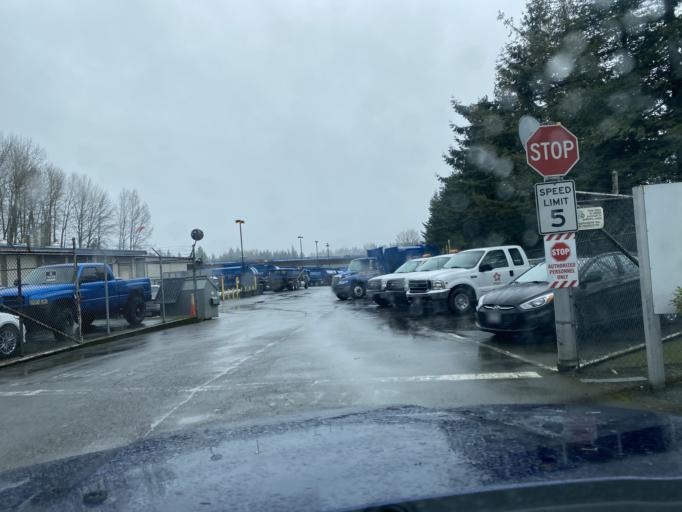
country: US
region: Washington
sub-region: King County
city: Bellevue
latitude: 47.6261
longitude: -122.1710
